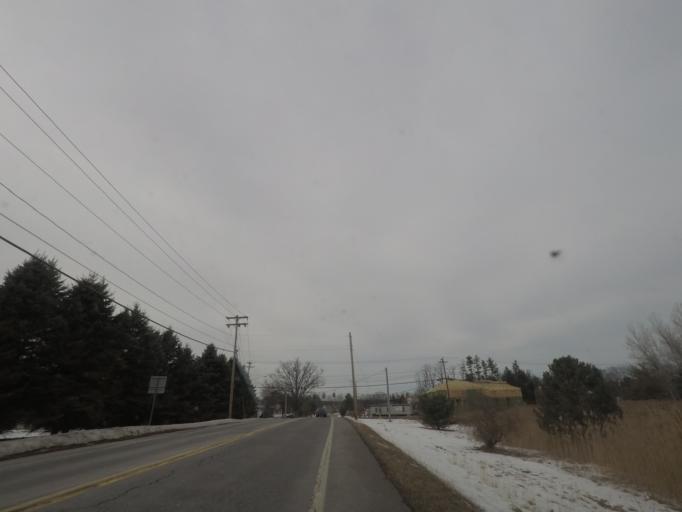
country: US
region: New York
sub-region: Albany County
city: Westmere
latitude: 42.6821
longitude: -73.9020
